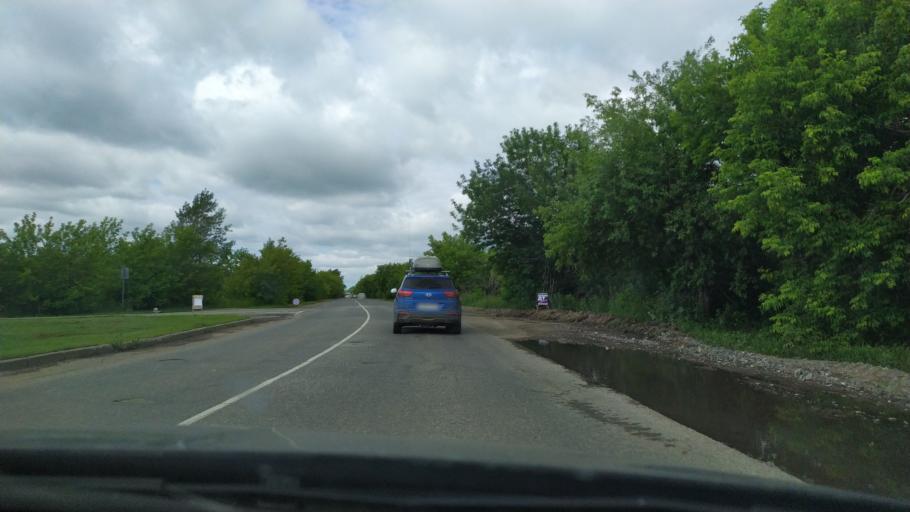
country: RU
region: Perm
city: Kondratovo
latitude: 57.9276
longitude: 56.1154
